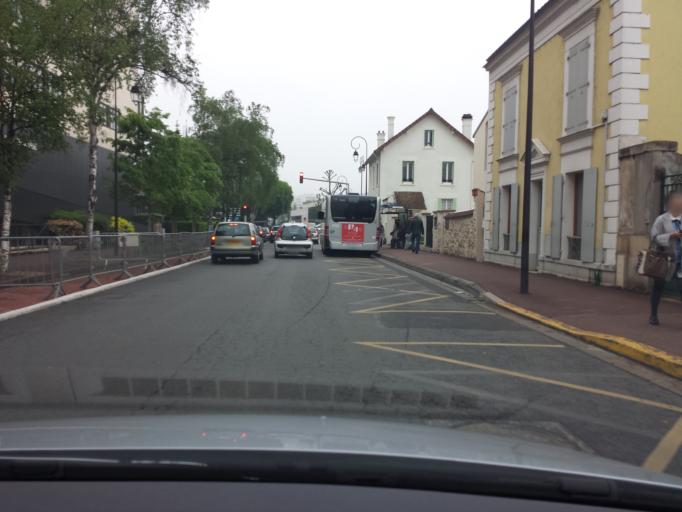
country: FR
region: Ile-de-France
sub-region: Departement des Hauts-de-Seine
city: Antony
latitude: 48.7536
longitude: 2.3000
